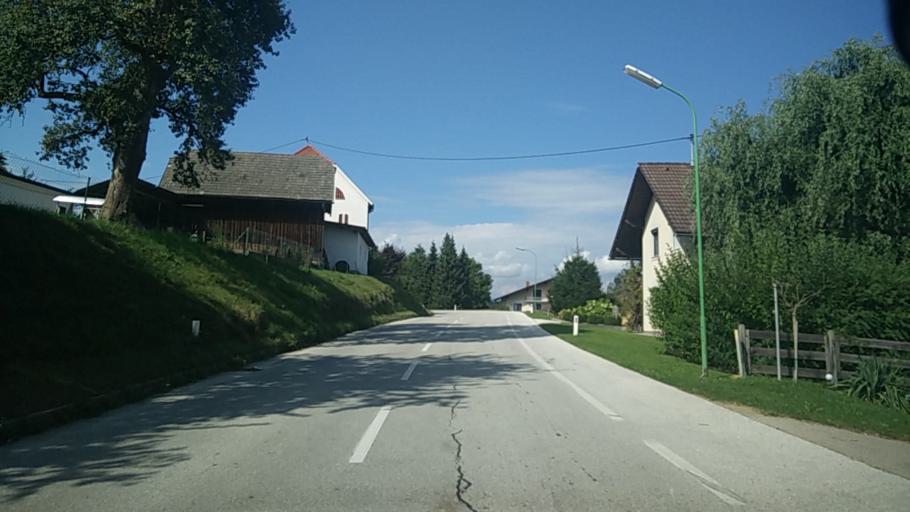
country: AT
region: Carinthia
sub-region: Politischer Bezirk Volkermarkt
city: Sittersdorf
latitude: 46.5624
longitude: 14.5681
